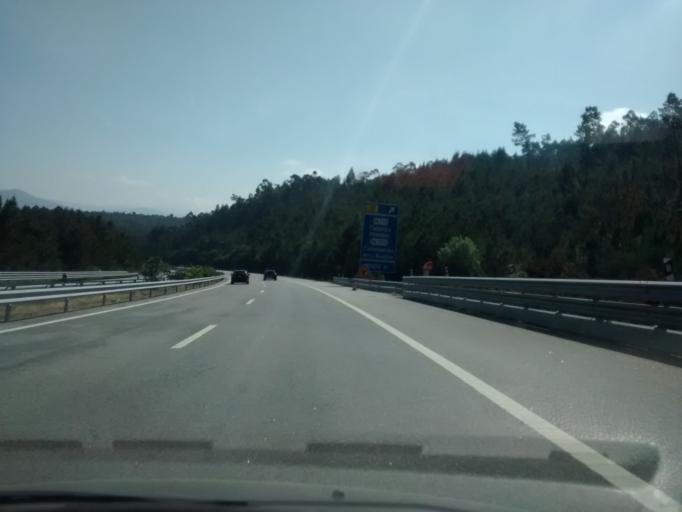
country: PT
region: Braga
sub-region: Cabeceiras de Basto
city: Cabeceiras de Basto
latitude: 41.4713
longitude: -7.9761
